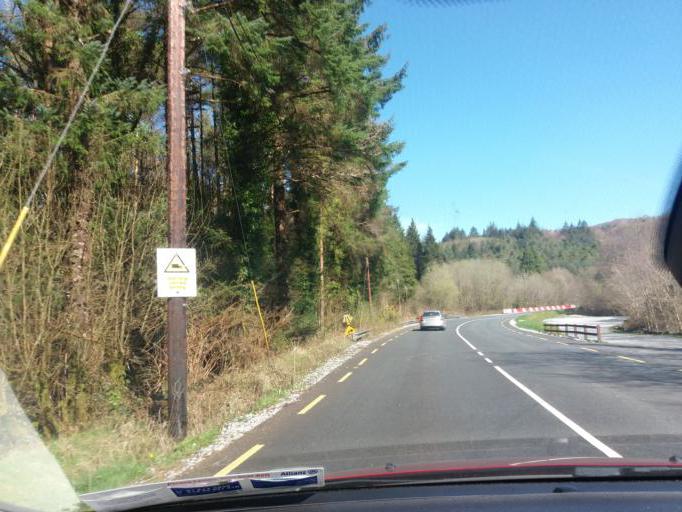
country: IE
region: Munster
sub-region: Ciarrai
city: Cill Airne
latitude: 51.9532
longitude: -9.3893
